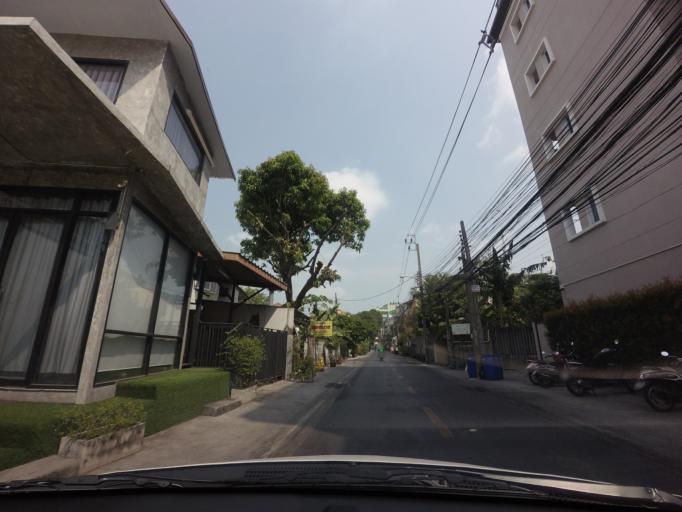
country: TH
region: Bangkok
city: Chatuchak
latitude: 13.8503
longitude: 100.5805
